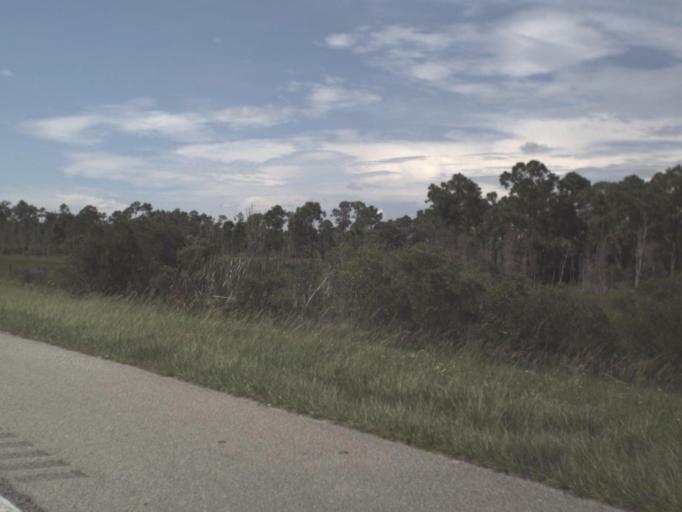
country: US
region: Florida
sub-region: Charlotte County
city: Charlotte Park
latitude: 26.8446
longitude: -81.9684
